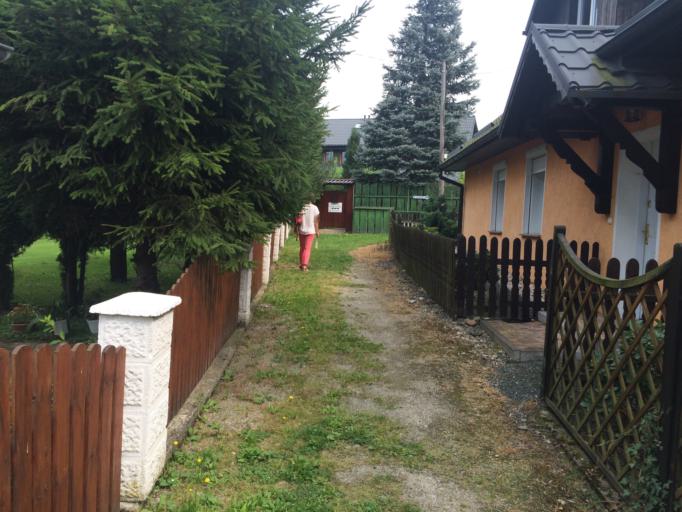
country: PL
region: Lower Silesian Voivodeship
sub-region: Powiat jeleniogorski
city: Sosnowka
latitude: 50.8197
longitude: 15.7222
